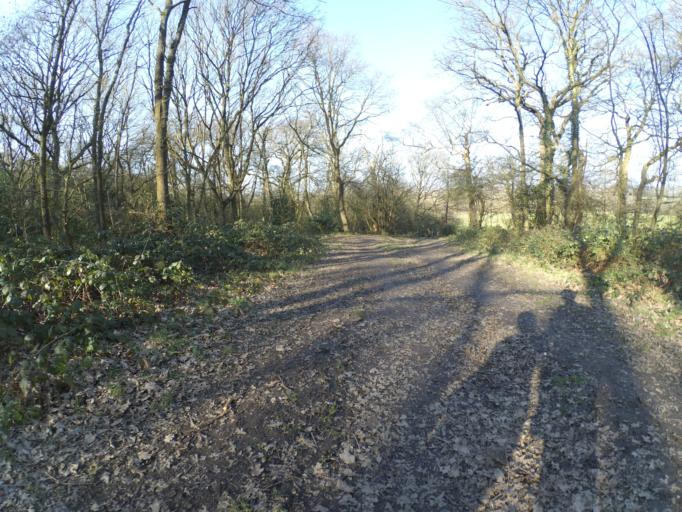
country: GB
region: England
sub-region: Greater London
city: Wembley
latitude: 51.5747
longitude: -0.2796
